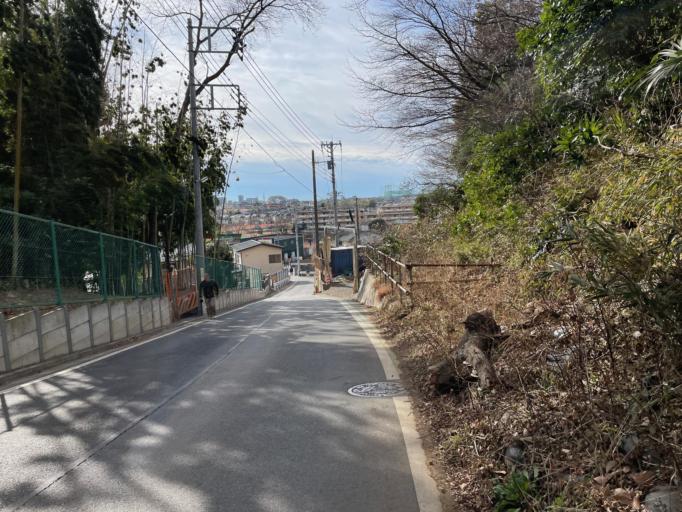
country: JP
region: Saitama
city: Tokorozawa
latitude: 35.7908
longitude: 139.5164
